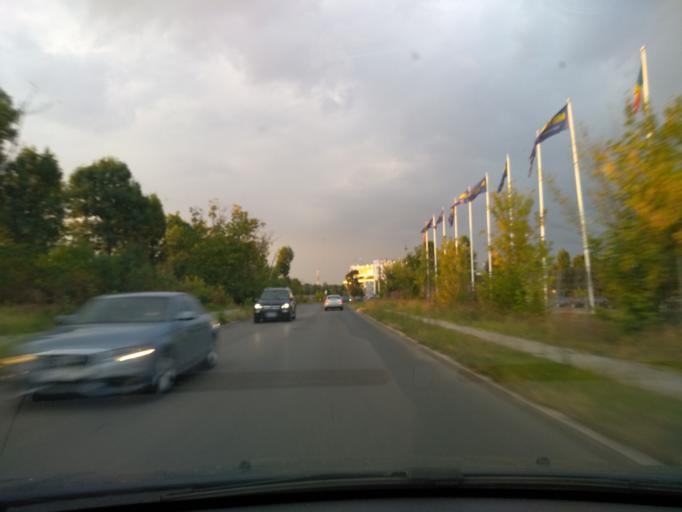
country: RO
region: Ilfov
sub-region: Comuna Otopeni
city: Otopeni
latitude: 44.5113
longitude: 26.0819
